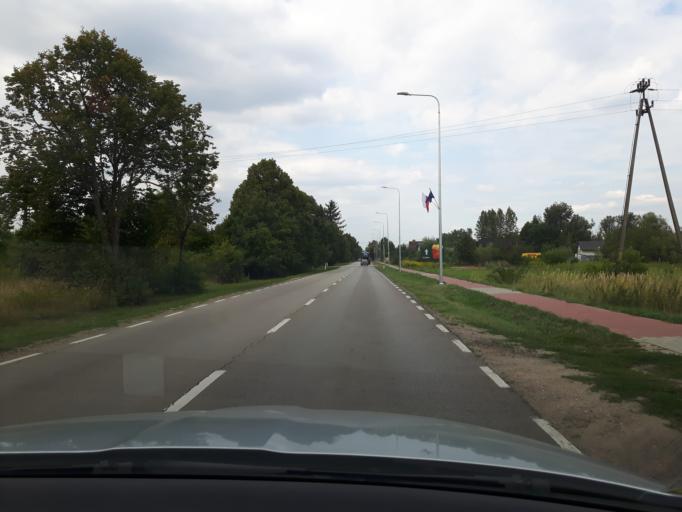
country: PL
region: Masovian Voivodeship
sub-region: Powiat legionowski
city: Nieporet
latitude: 52.4111
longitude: 21.0382
